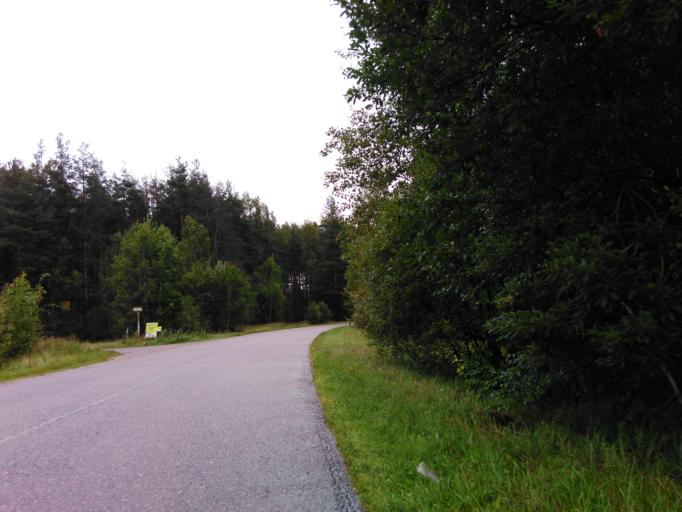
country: RU
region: Moskovskaya
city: Pavlovskiy Posad
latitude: 55.9387
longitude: 38.6333
